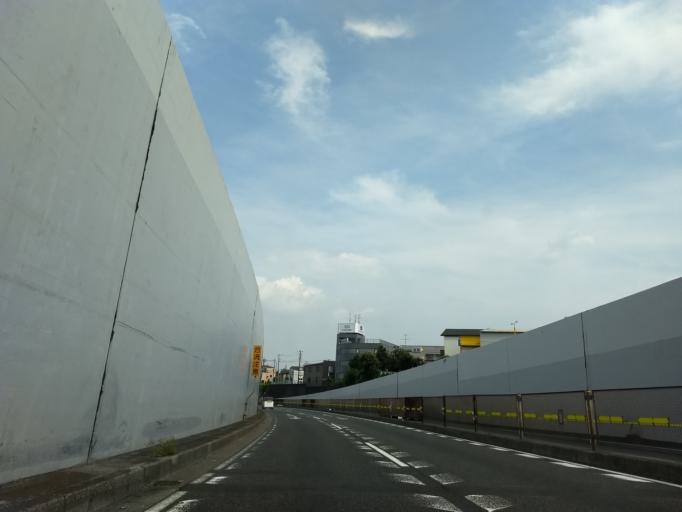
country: JP
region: Tokyo
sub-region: Machida-shi
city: Machida
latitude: 35.5147
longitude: 139.4575
